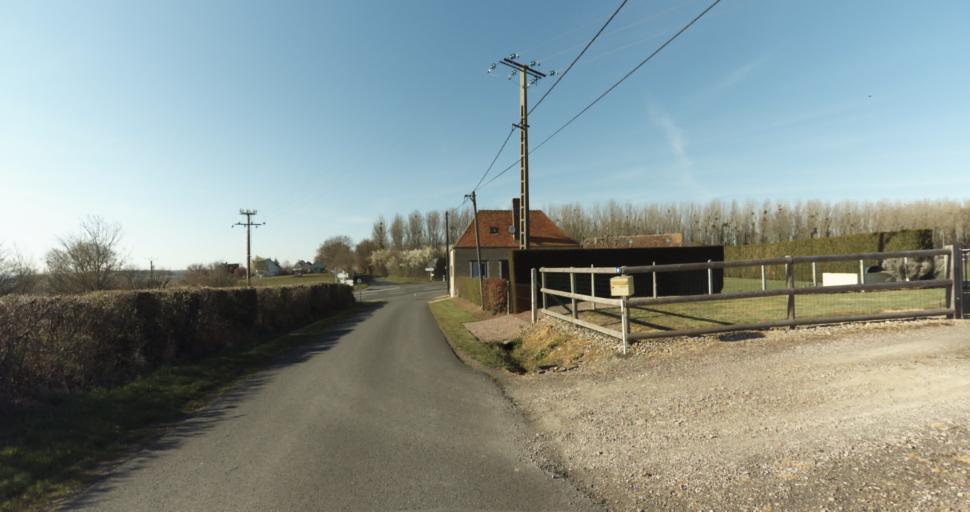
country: FR
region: Lower Normandy
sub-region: Departement du Calvados
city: Saint-Pierre-sur-Dives
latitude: 49.0492
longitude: 0.0291
